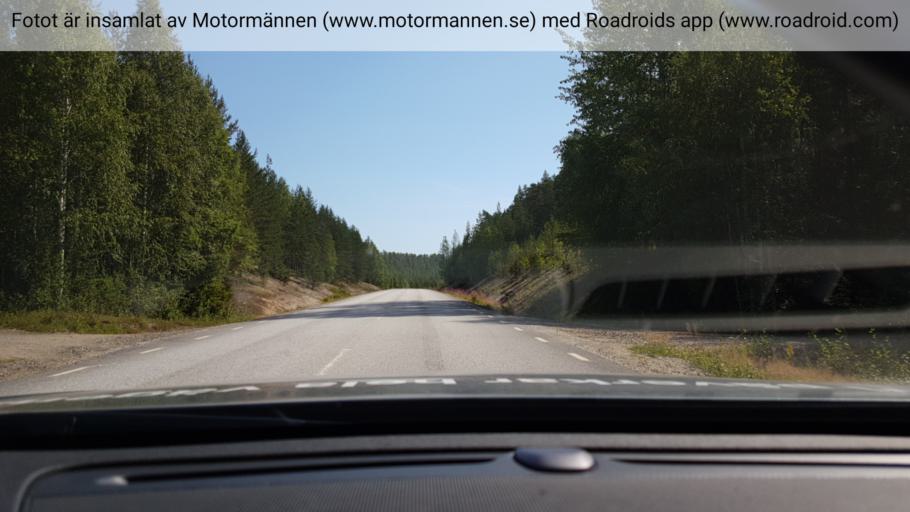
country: SE
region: Vaesterbotten
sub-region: Vindelns Kommun
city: Vindeln
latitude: 64.3168
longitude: 19.5757
